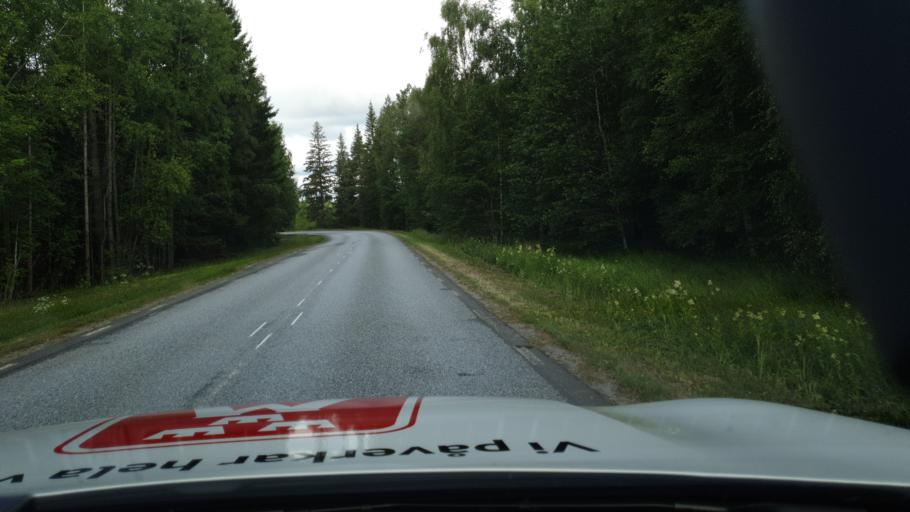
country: SE
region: Vaesterbotten
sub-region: Umea Kommun
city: Hoernefors
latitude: 63.6816
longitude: 20.0374
